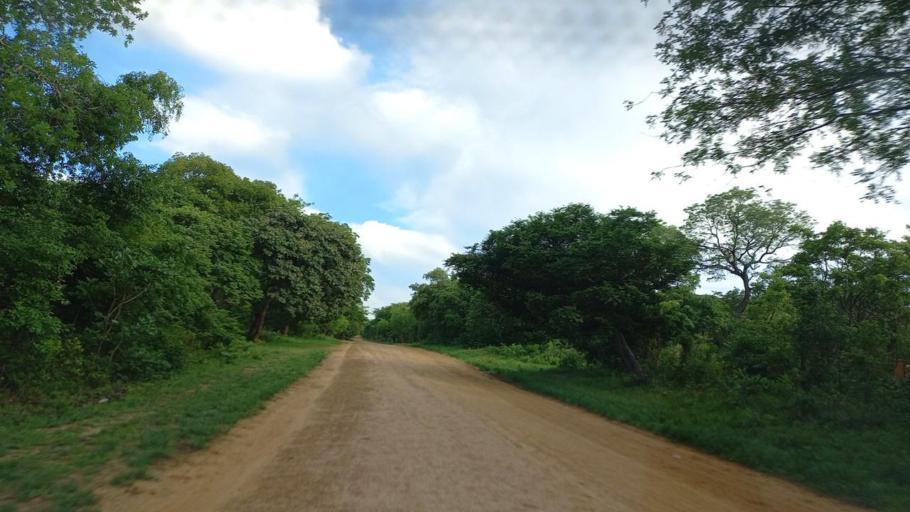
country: ZM
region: North-Western
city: Kabompo
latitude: -13.3716
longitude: 24.2973
